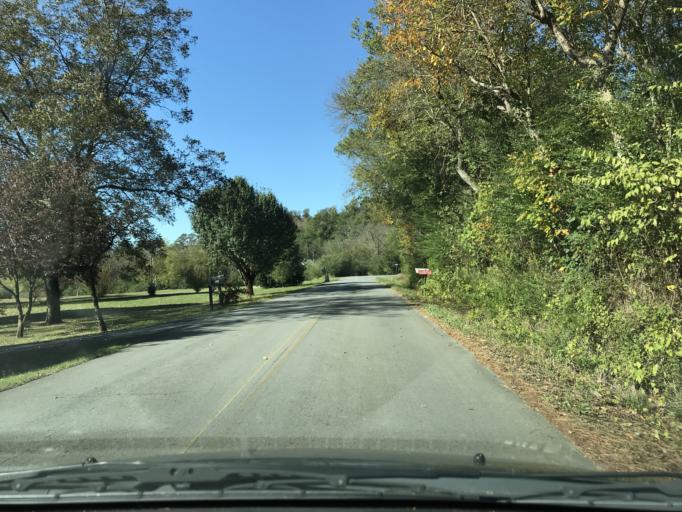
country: US
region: Georgia
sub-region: Dade County
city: Trenton
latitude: 34.9018
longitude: -85.4618
